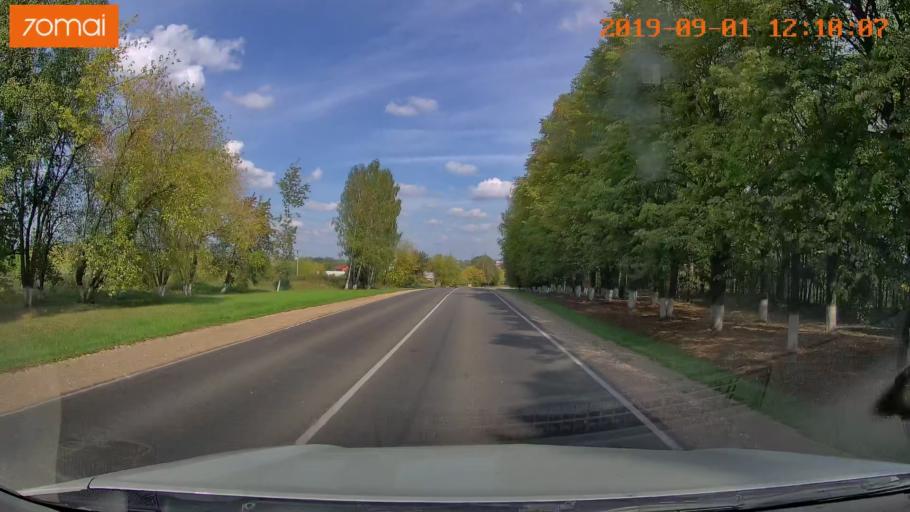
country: RU
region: Kaluga
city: Maloyaroslavets
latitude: 54.9881
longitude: 36.4306
